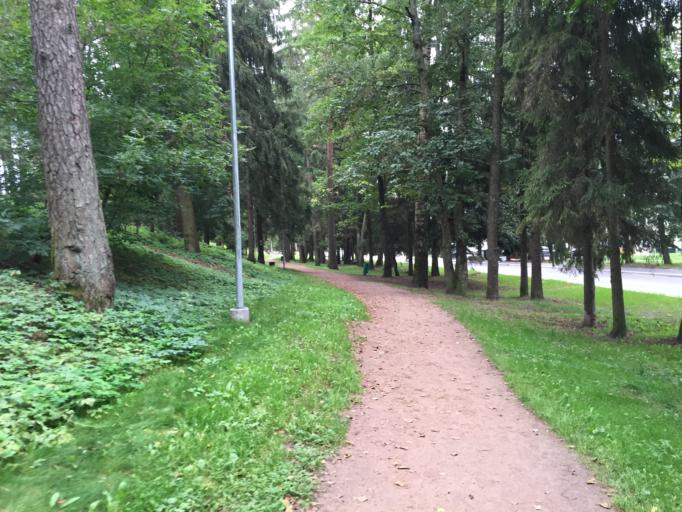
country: LV
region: Ogre
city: Ogre
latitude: 56.8259
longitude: 24.5954
